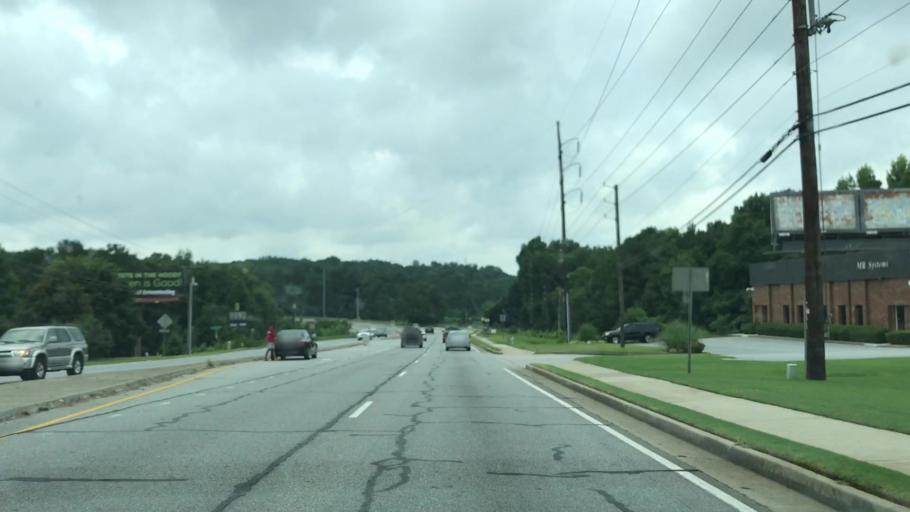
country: US
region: Georgia
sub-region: Gwinnett County
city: Lilburn
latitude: 33.9236
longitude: -84.1385
